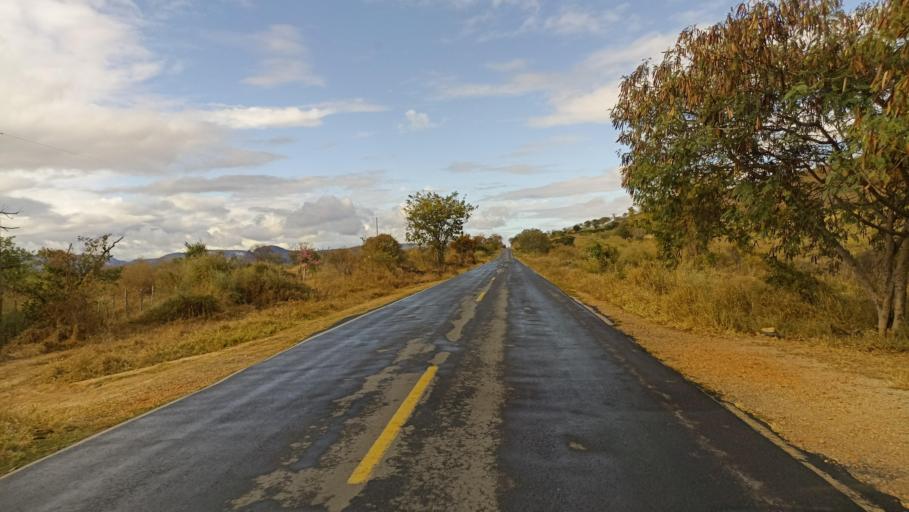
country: BR
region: Minas Gerais
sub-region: Itinga
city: Itinga
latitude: -16.5866
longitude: -41.6690
